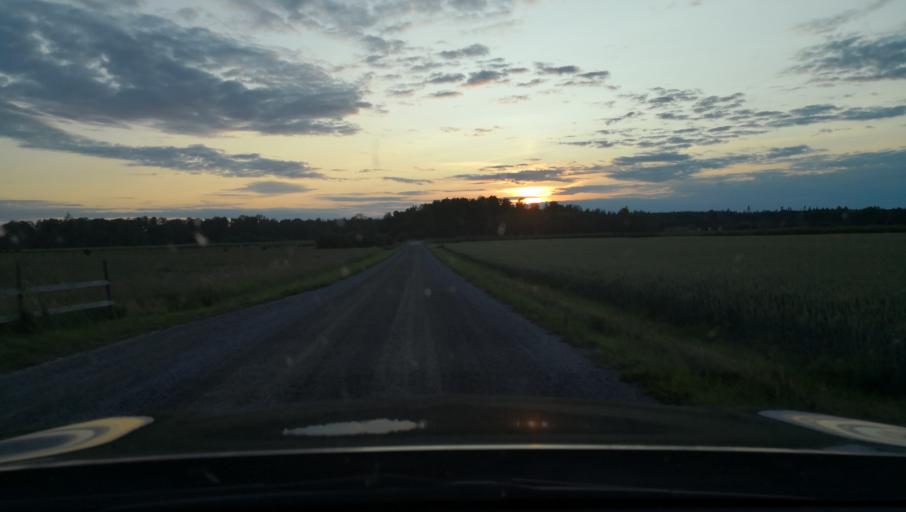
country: SE
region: Uppsala
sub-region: Osthammars Kommun
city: Bjorklinge
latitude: 60.0592
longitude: 17.5856
